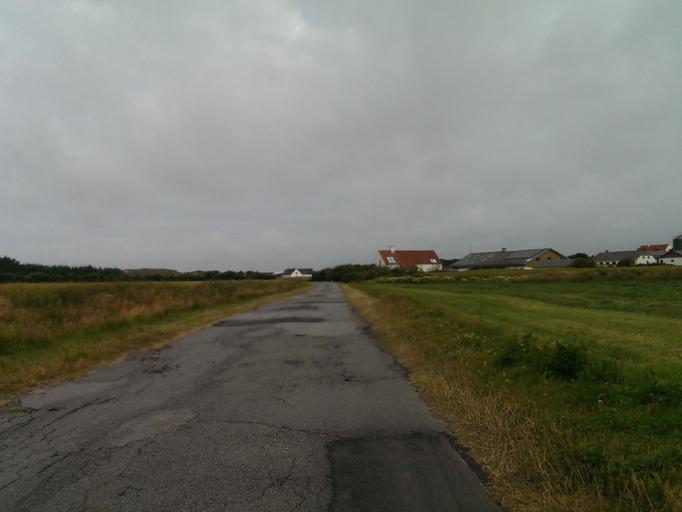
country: DK
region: North Denmark
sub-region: Jammerbugt Kommune
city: Pandrup
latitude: 57.3795
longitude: 9.7340
